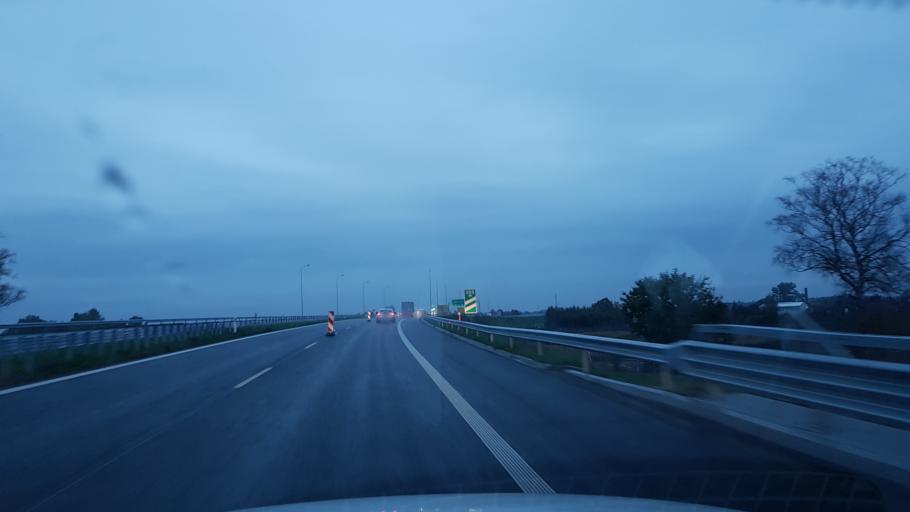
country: PL
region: West Pomeranian Voivodeship
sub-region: Powiat gryficki
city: Ploty
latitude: 53.8127
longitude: 15.2486
